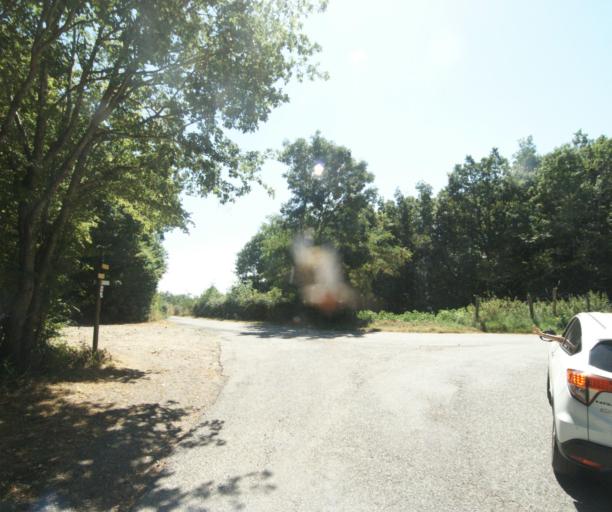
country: FR
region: Rhone-Alpes
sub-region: Departement du Rhone
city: Bessenay
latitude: 45.7777
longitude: 4.5117
